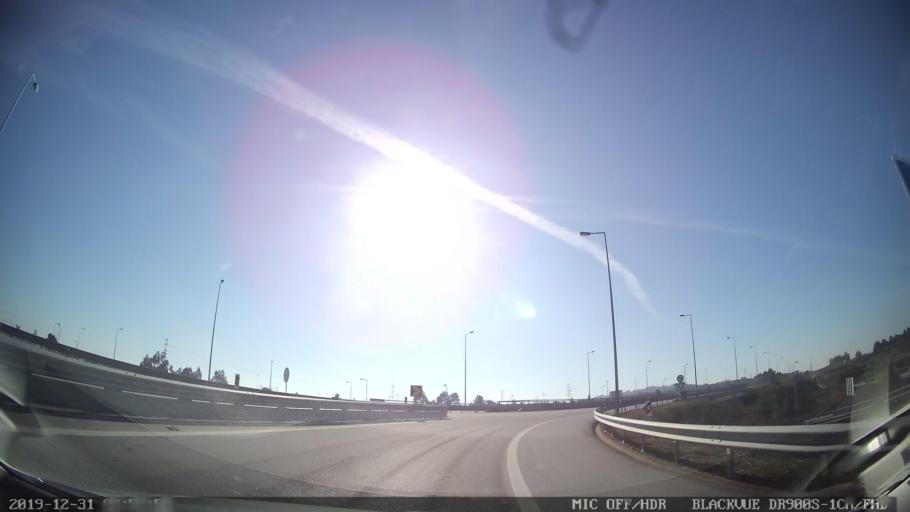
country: PT
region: Castelo Branco
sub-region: Castelo Branco
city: Castelo Branco
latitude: 39.7869
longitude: -7.5697
